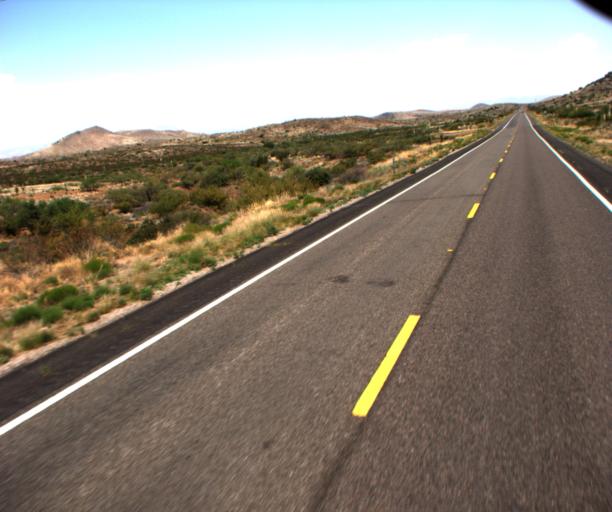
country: US
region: Arizona
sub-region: Greenlee County
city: Clifton
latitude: 32.7730
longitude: -109.2770
